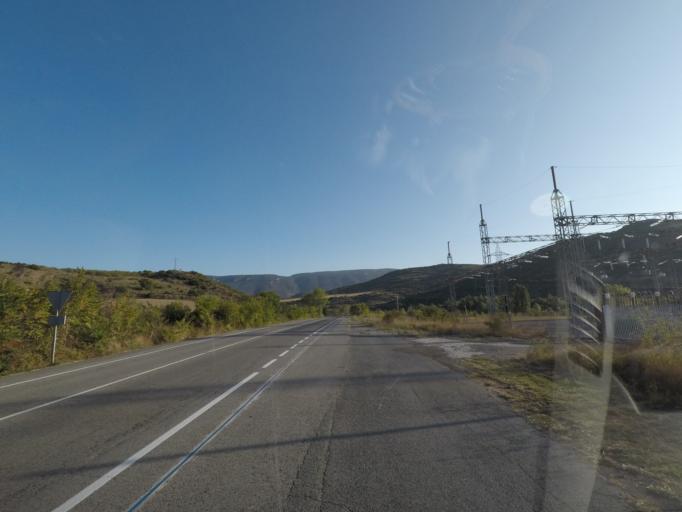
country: ES
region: Navarre
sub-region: Provincia de Navarra
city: Liedena
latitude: 42.5984
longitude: -1.2770
